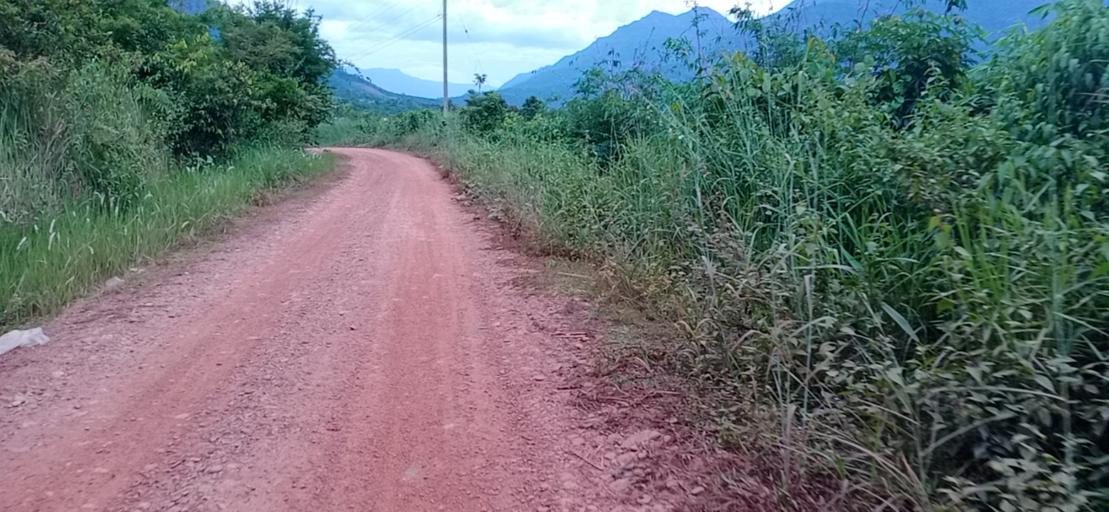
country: TH
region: Changwat Bueng Kan
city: Pak Khat
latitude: 18.5526
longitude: 103.1673
